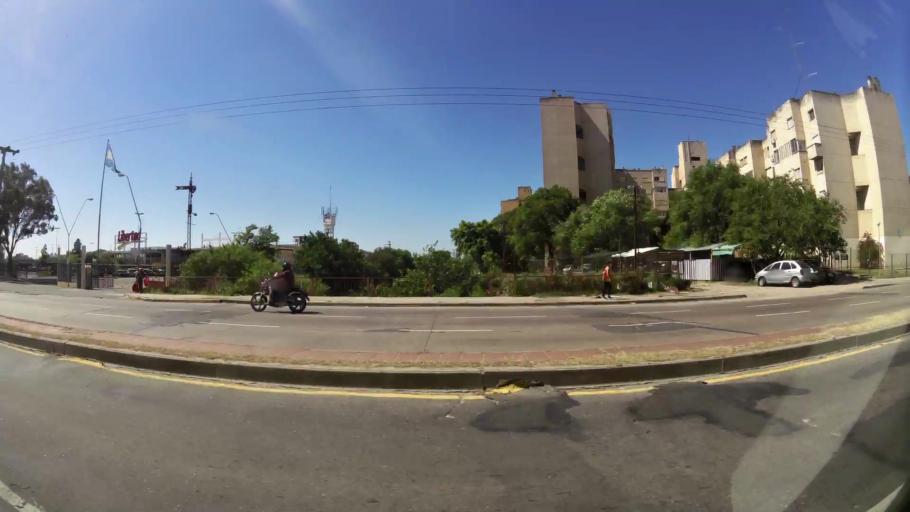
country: AR
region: Cordoba
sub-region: Departamento de Capital
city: Cordoba
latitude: -31.4331
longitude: -64.1450
